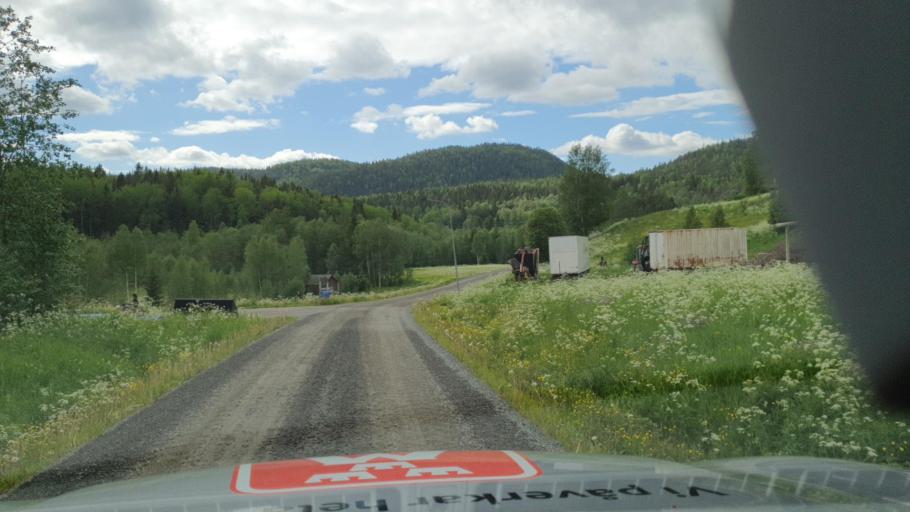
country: SE
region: Vaesternorrland
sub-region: Kramfors Kommun
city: Nordingra
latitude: 62.9028
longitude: 18.2529
